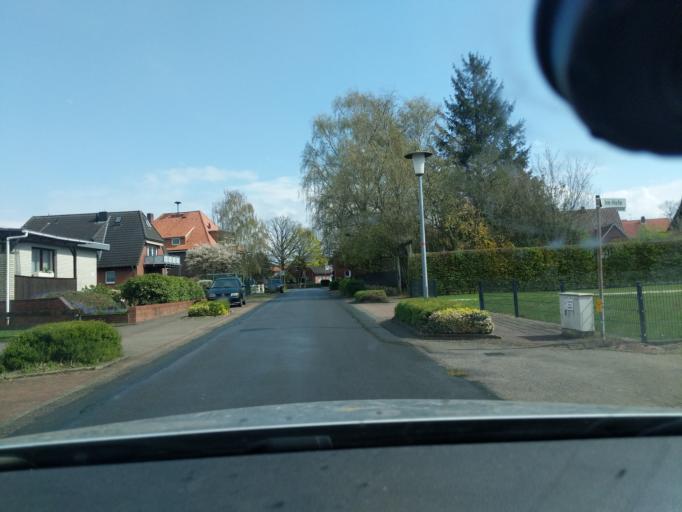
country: DE
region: Lower Saxony
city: Ahlerstedt
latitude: 53.4033
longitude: 9.4488
